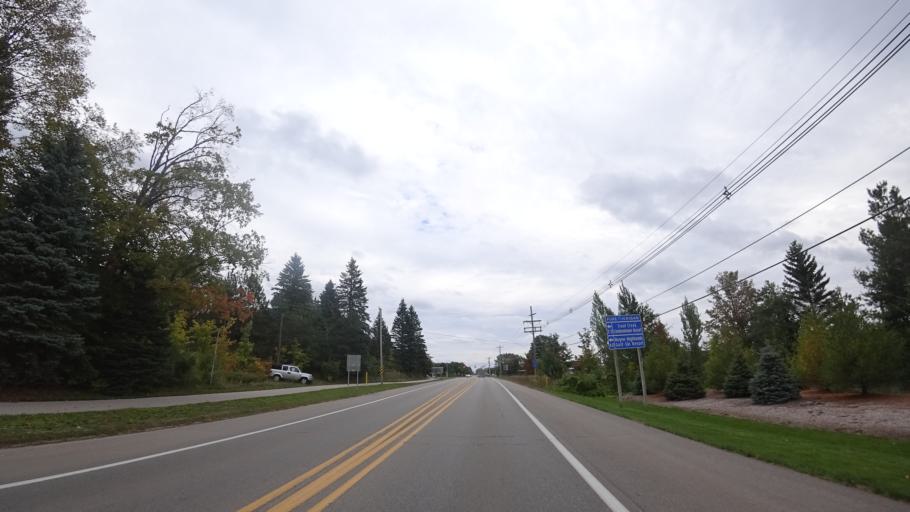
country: US
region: Michigan
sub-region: Emmet County
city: Petoskey
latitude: 45.4279
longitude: -84.9154
